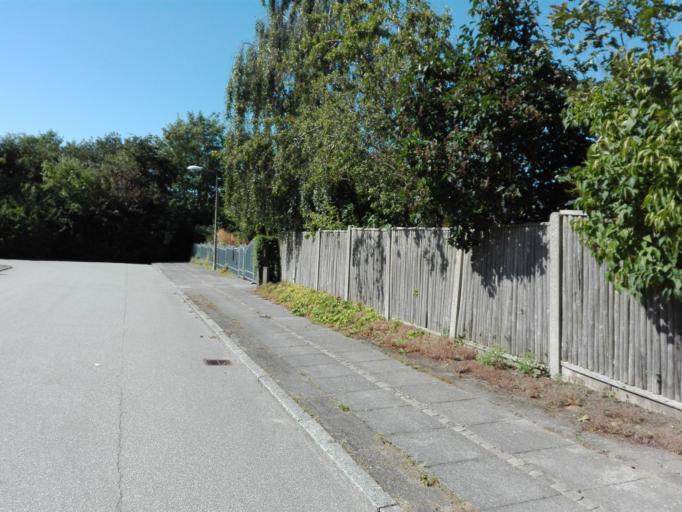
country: DK
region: Central Jutland
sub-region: Arhus Kommune
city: Stavtrup
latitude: 56.1123
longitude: 10.1436
